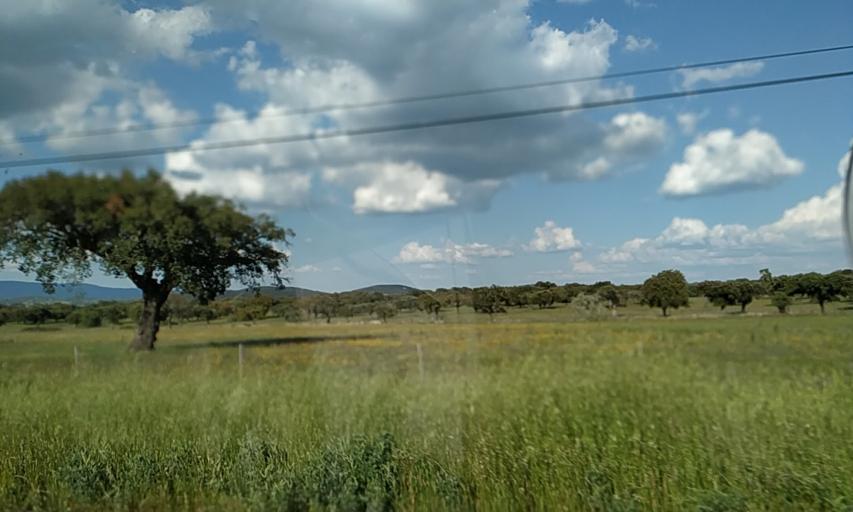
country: PT
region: Portalegre
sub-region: Portalegre
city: Urra
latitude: 39.1832
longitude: -7.4552
